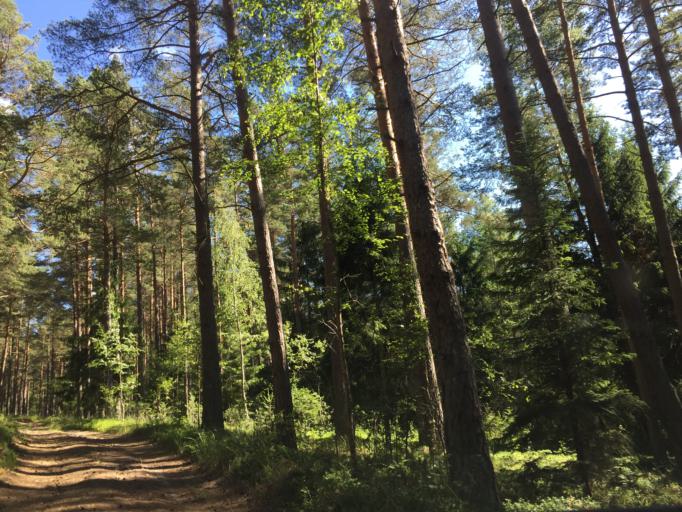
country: LV
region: Ventspils
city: Ventspils
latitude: 57.4673
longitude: 21.6514
